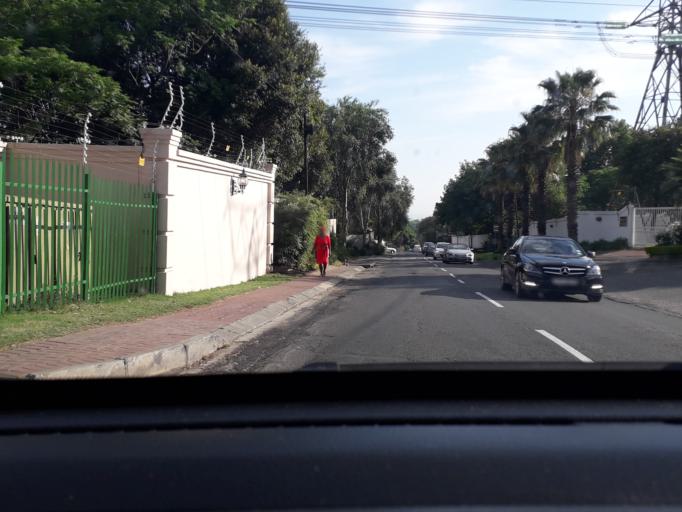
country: ZA
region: Gauteng
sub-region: City of Johannesburg Metropolitan Municipality
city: Modderfontein
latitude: -26.0861
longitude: 28.0562
